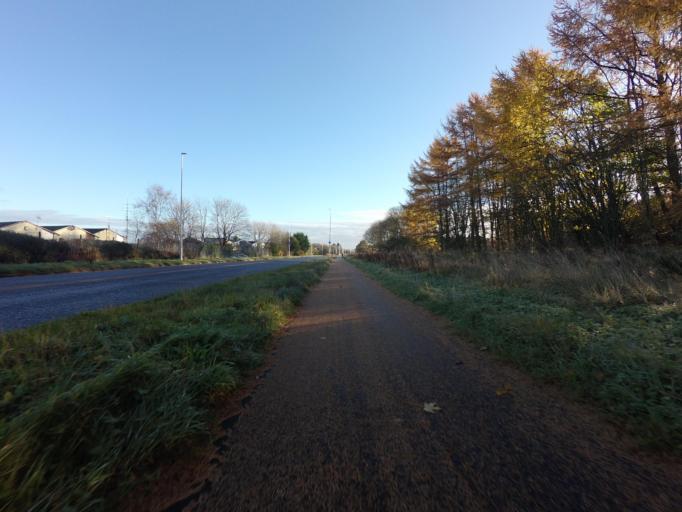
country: GB
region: Scotland
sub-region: West Lothian
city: Livingston
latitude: 55.9197
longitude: -3.5381
